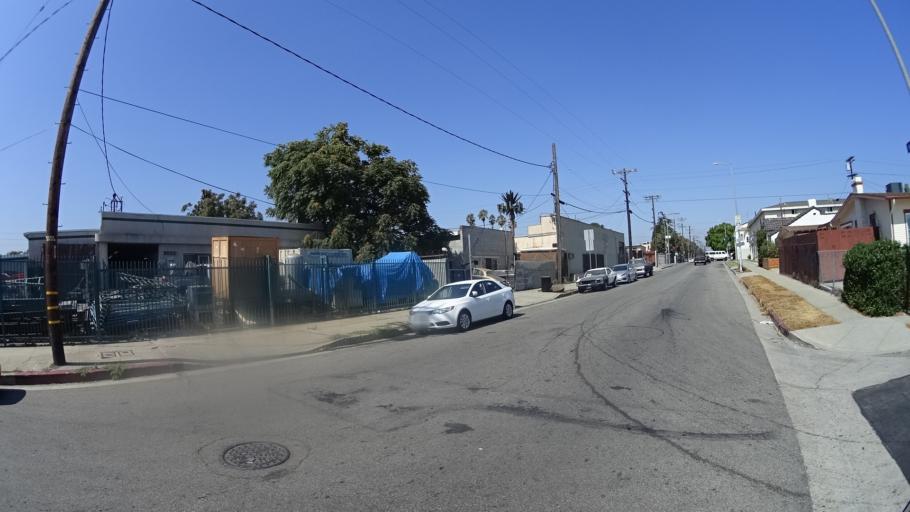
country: US
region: California
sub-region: Los Angeles County
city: View Park-Windsor Hills
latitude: 33.9807
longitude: -118.3255
